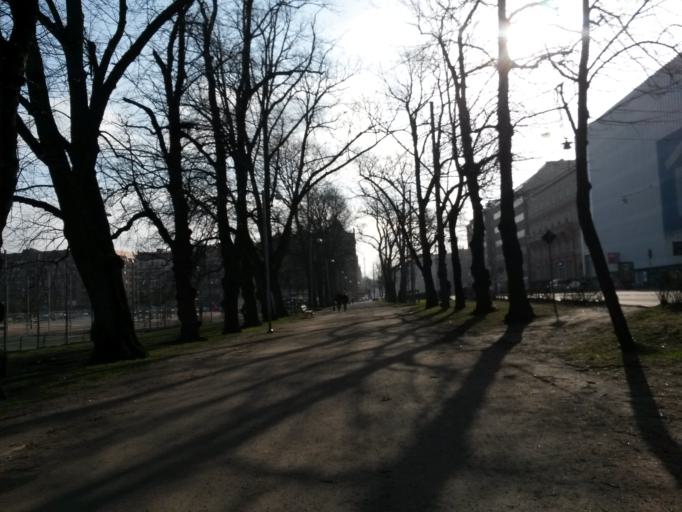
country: SE
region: Vaestra Goetaland
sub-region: Goteborg
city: Goeteborg
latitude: 57.7008
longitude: 11.9775
